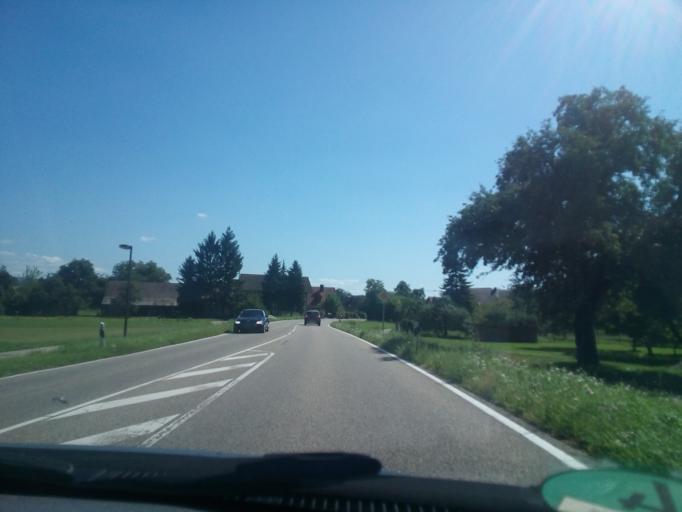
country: DE
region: Baden-Wuerttemberg
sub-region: Karlsruhe Region
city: Lichtenau
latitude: 48.7323
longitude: 8.0085
